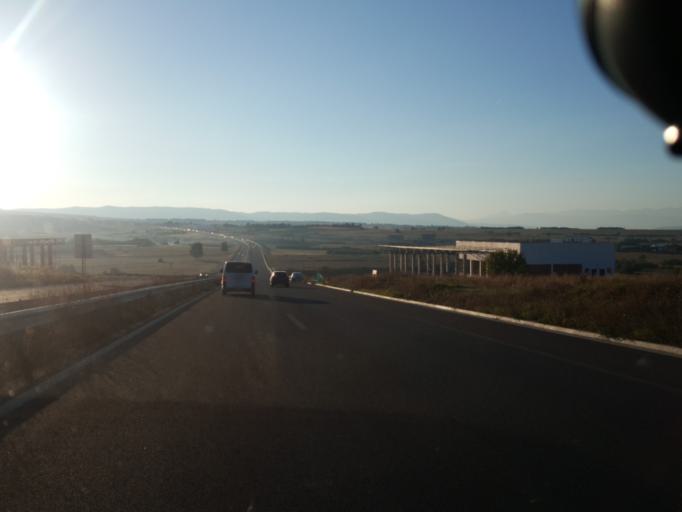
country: XK
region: Prizren
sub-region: Komuna e Malisheves
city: Llazice
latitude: 42.5740
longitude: 20.7260
